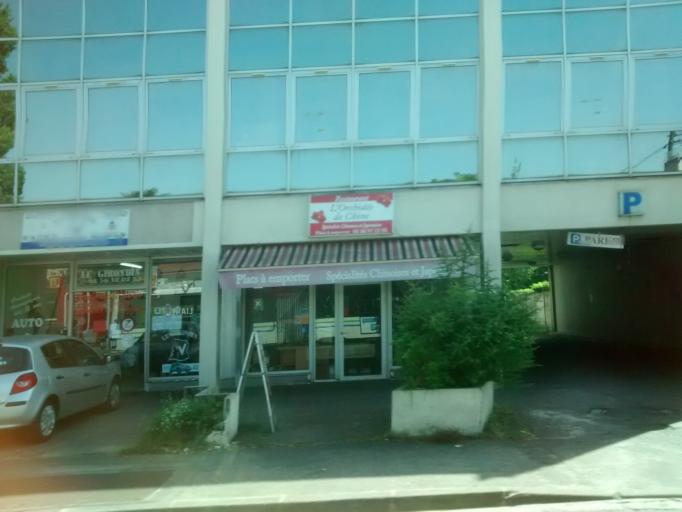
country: FR
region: Aquitaine
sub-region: Departement de la Gironde
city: Merignac
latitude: 44.8409
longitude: -0.6424
